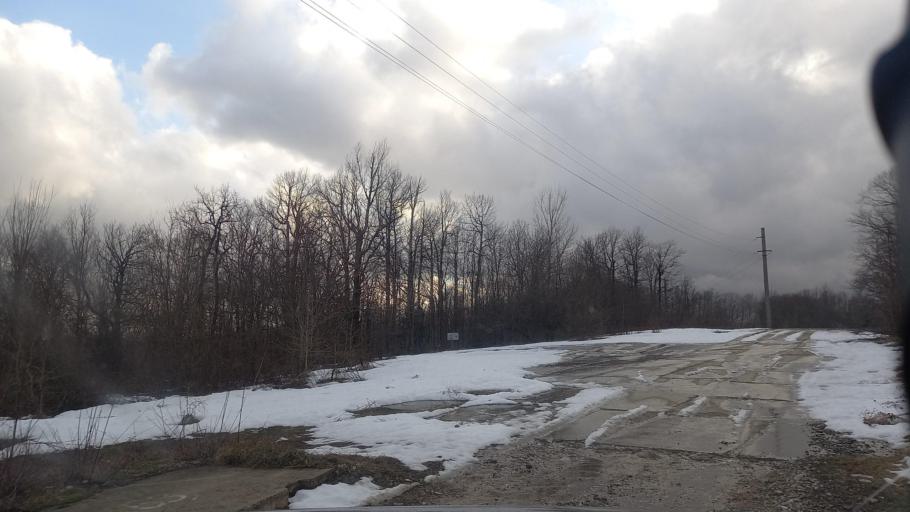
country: RU
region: Krasnodarskiy
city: Dzhubga
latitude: 44.5064
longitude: 38.7699
